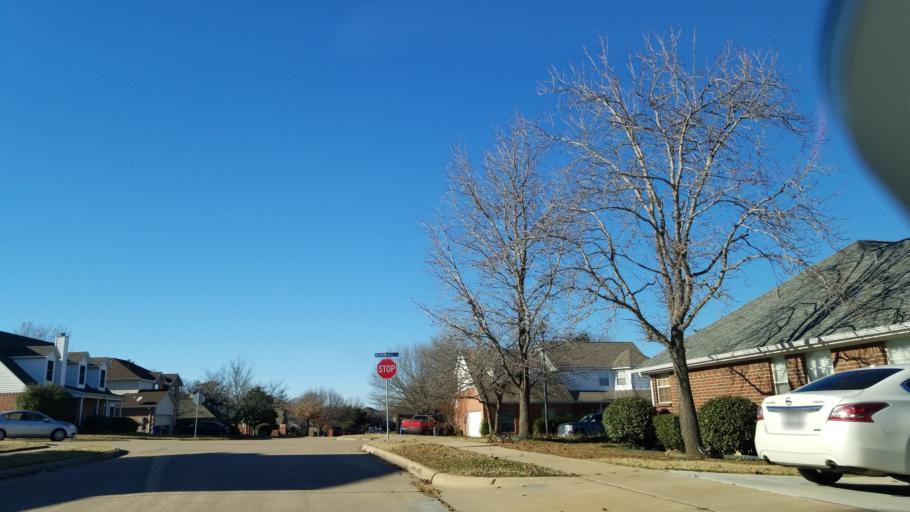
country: US
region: Texas
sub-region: Denton County
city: Corinth
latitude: 33.1362
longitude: -97.0786
